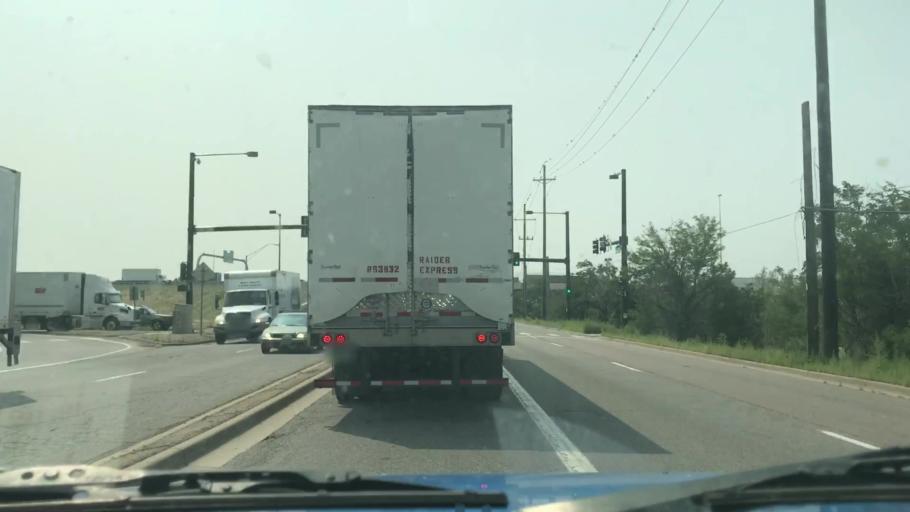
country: US
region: Colorado
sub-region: Adams County
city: Aurora
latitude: 39.7777
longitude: -104.8659
